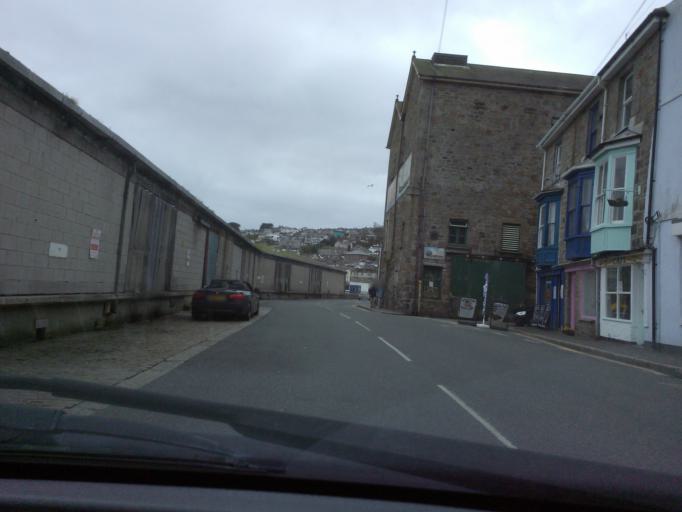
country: GB
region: England
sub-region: Cornwall
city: Penzance
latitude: 50.1056
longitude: -5.5493
